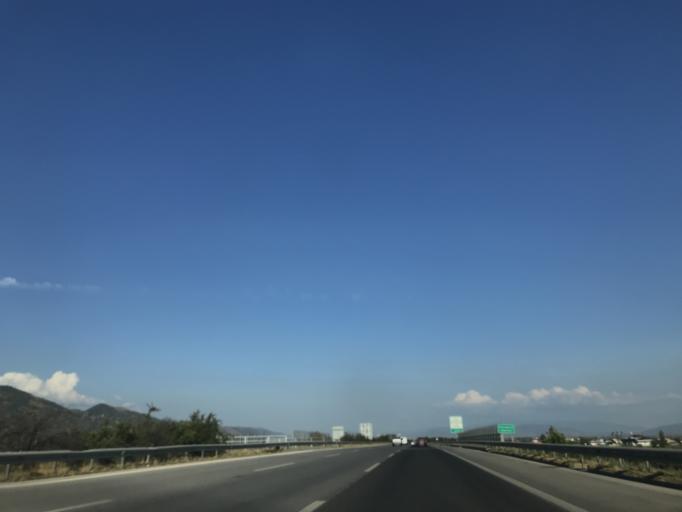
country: TR
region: Aydin
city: Germencik
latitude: 37.8809
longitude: 27.5911
